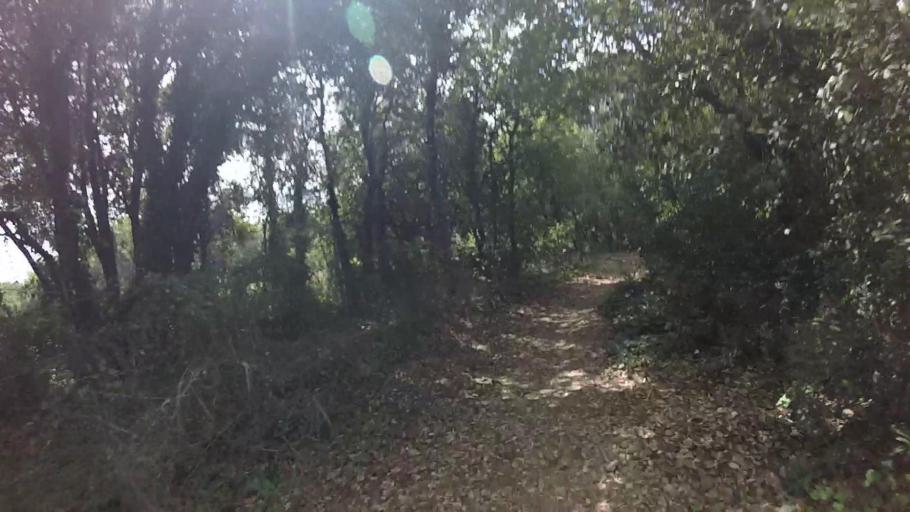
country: FR
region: Provence-Alpes-Cote d'Azur
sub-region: Departement des Alpes-Maritimes
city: Biot
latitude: 43.6226
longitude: 7.0679
